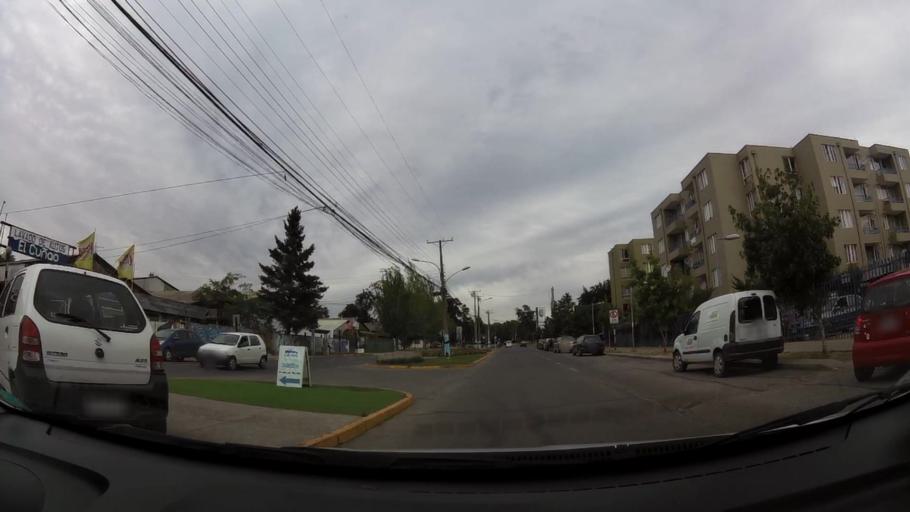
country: CL
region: O'Higgins
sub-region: Provincia de Cachapoal
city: Rancagua
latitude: -34.1385
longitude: -70.7377
